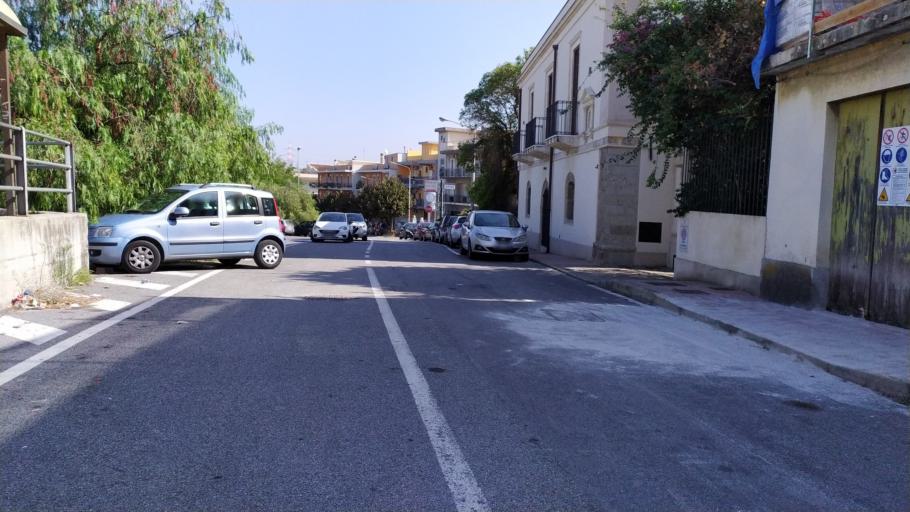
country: IT
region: Sicily
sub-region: Messina
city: San Filippo del Mela
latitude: 38.1799
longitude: 15.2673
